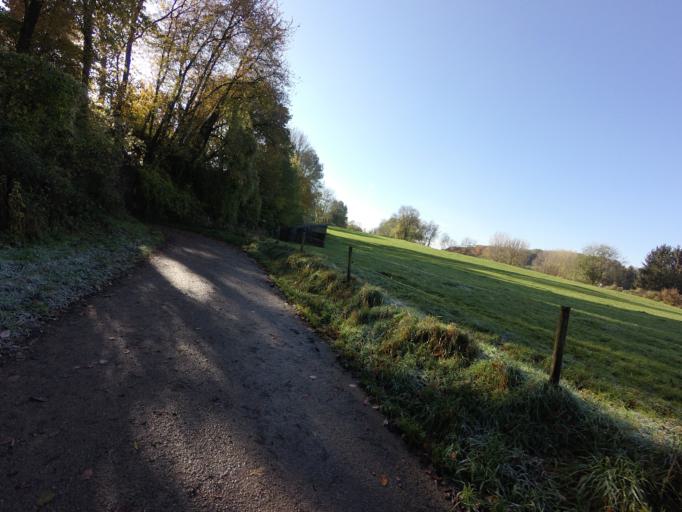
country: NL
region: Limburg
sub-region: Gemeente Simpelveld
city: Simpelveld
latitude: 50.8276
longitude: 5.9641
